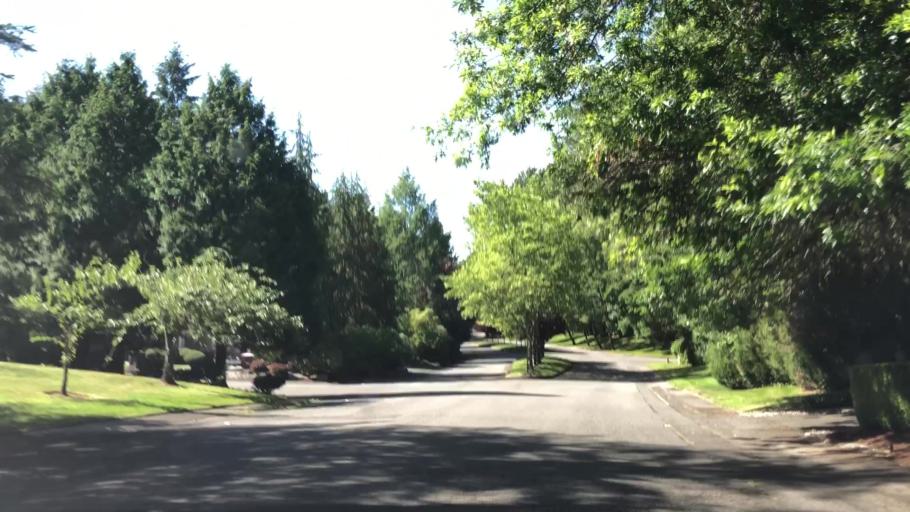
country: US
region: Washington
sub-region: King County
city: Cottage Lake
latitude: 47.7144
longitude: -122.0733
